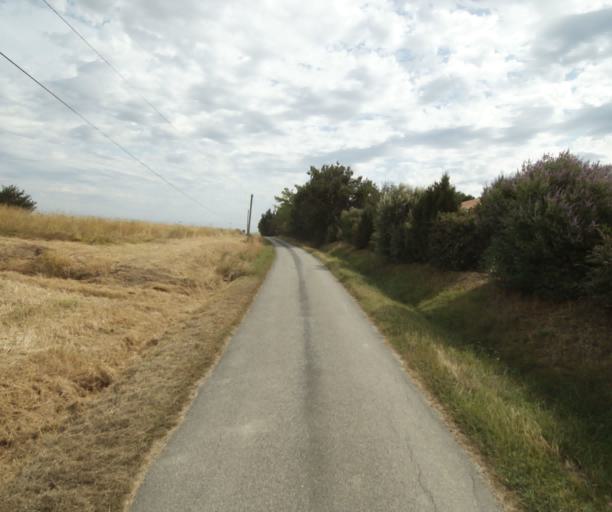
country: FR
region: Midi-Pyrenees
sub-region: Departement de la Haute-Garonne
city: Saint-Felix-Lauragais
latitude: 43.4385
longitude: 1.9290
